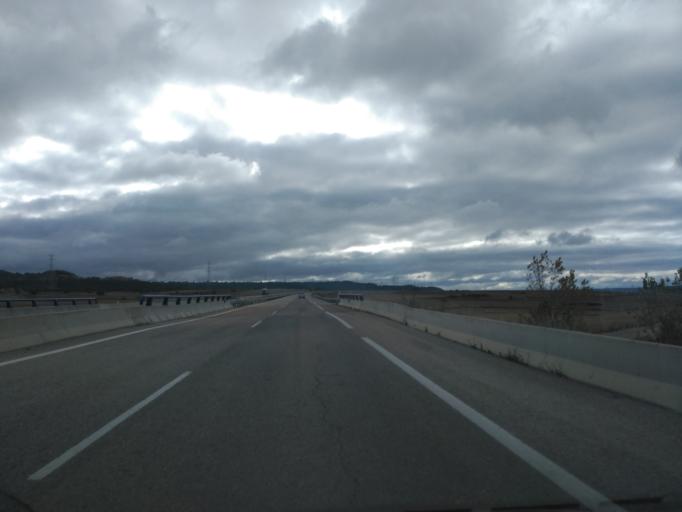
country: ES
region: Castille and Leon
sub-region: Provincia de Palencia
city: Villalobon
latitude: 42.0472
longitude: -4.4907
